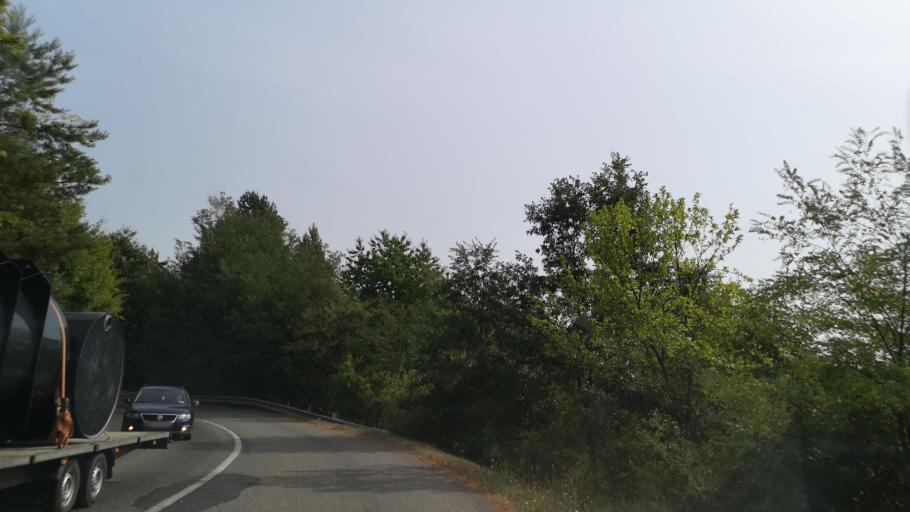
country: SK
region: Banskobystricky
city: Revuca
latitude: 48.5820
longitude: 20.0804
